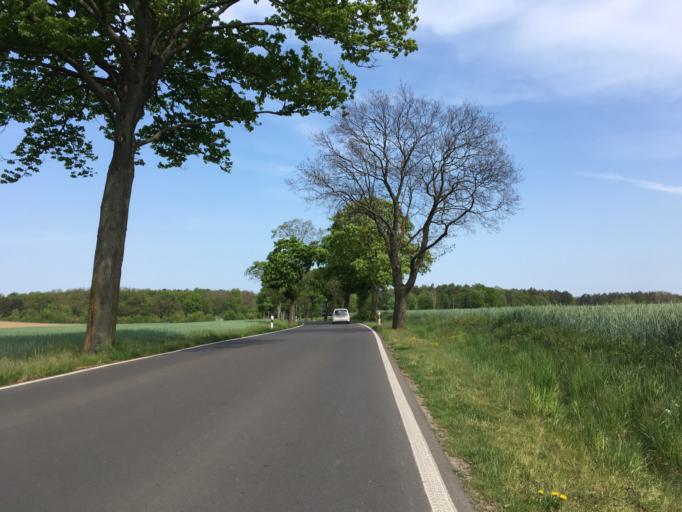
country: DE
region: Brandenburg
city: Werneuchen
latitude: 52.6091
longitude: 13.7574
